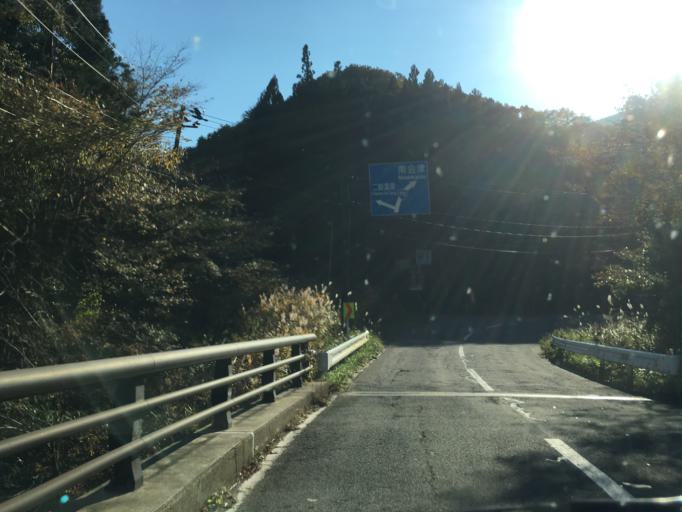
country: JP
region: Fukushima
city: Inawashiro
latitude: 37.2798
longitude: 139.9846
